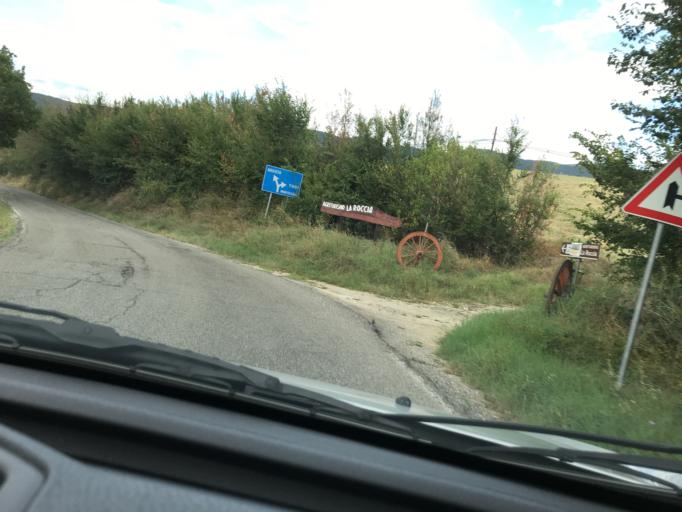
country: IT
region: Umbria
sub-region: Provincia di Terni
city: Montecchio
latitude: 42.6509
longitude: 12.2790
